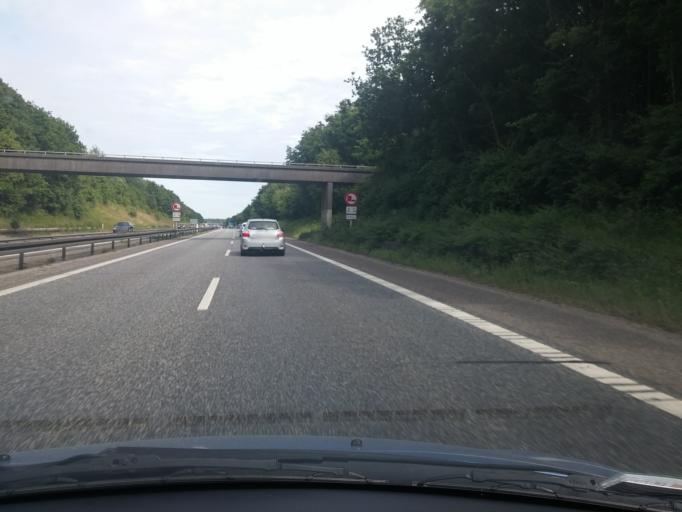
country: DK
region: South Denmark
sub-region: Odense Kommune
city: Odense
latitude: 55.3518
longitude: 10.3881
